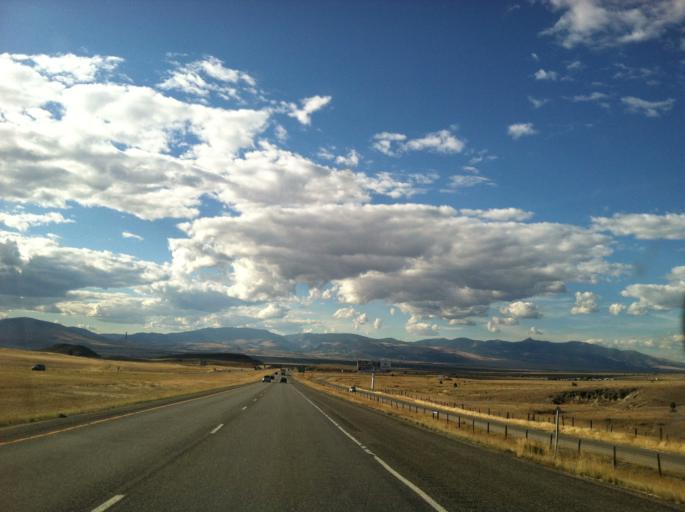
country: US
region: Montana
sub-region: Deer Lodge County
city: Warm Springs
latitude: 46.0490
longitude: -112.7491
